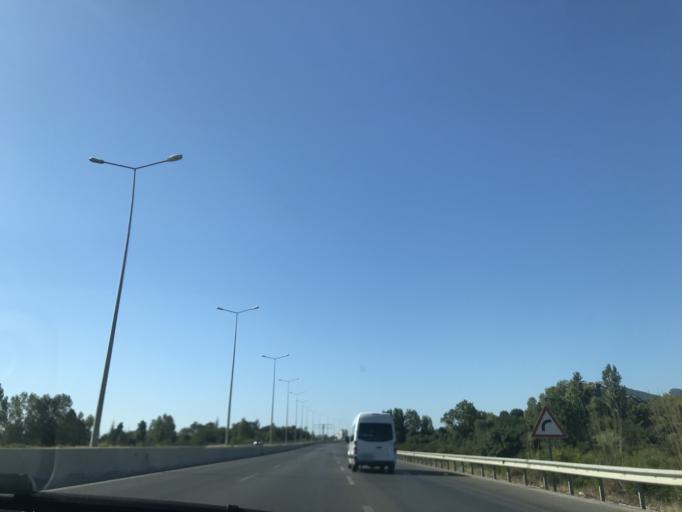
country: TR
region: Antalya
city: Cakirlar
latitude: 36.8765
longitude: 30.6098
